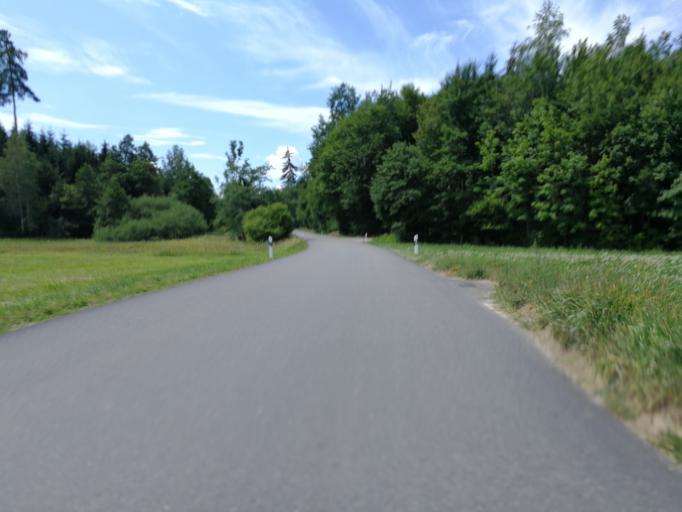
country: CH
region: Zurich
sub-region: Bezirk Hinwil
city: Hinwil
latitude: 47.2961
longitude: 8.8285
